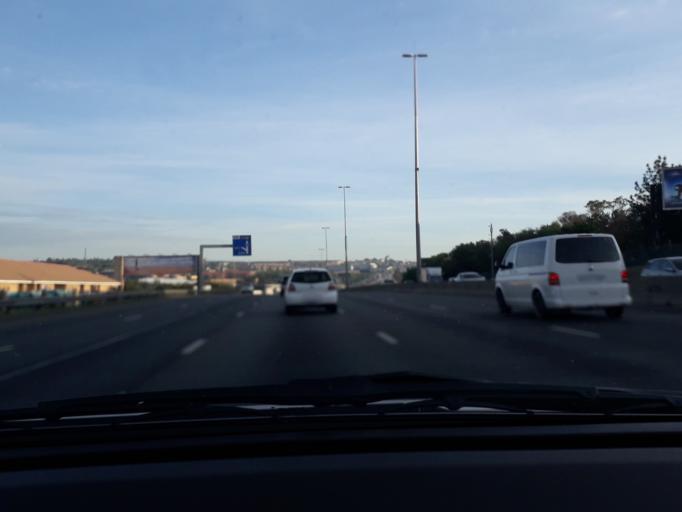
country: ZA
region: Gauteng
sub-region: City of Johannesburg Metropolitan Municipality
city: Midrand
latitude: -26.0009
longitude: 28.1211
